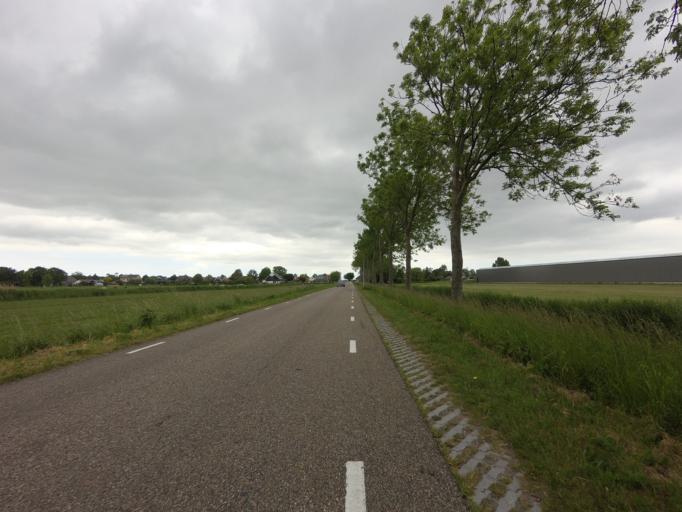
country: NL
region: North Holland
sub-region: Gemeente Hoorn
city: Hoorn
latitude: 52.6388
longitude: 5.0102
